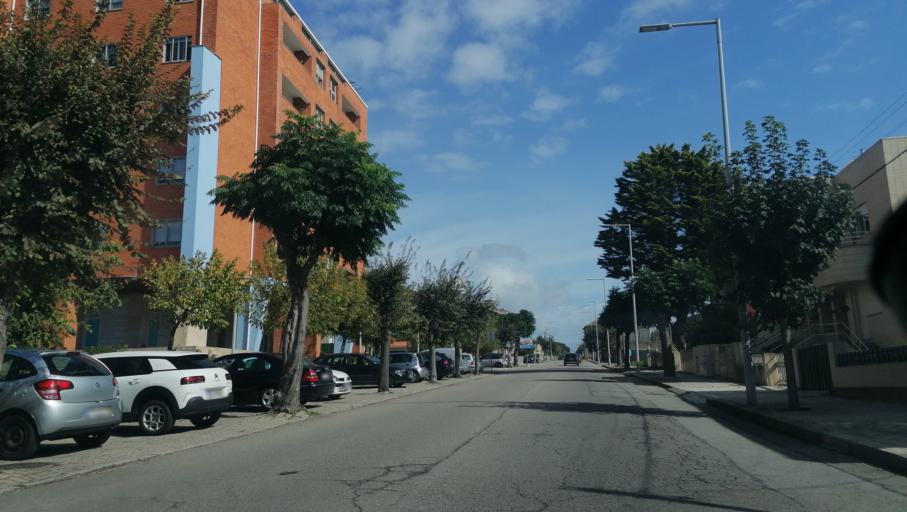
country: PT
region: Aveiro
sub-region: Espinho
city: Espinho
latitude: 41.0040
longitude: -8.6316
